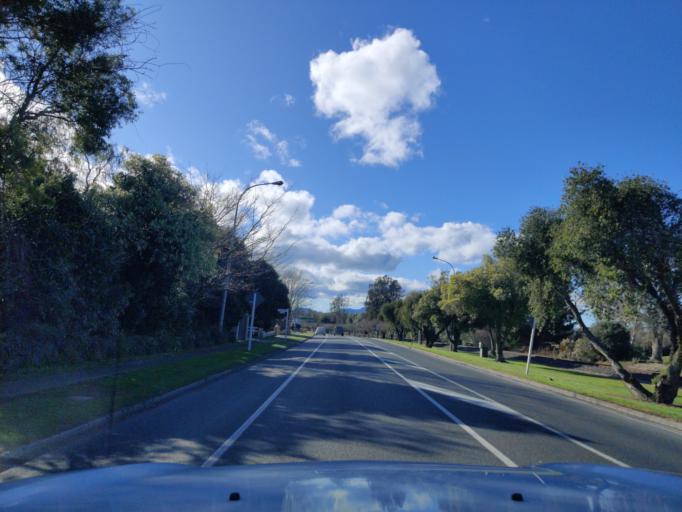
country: NZ
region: Waikato
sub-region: Matamata-Piako District
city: Matamata
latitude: -37.8245
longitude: 175.7702
